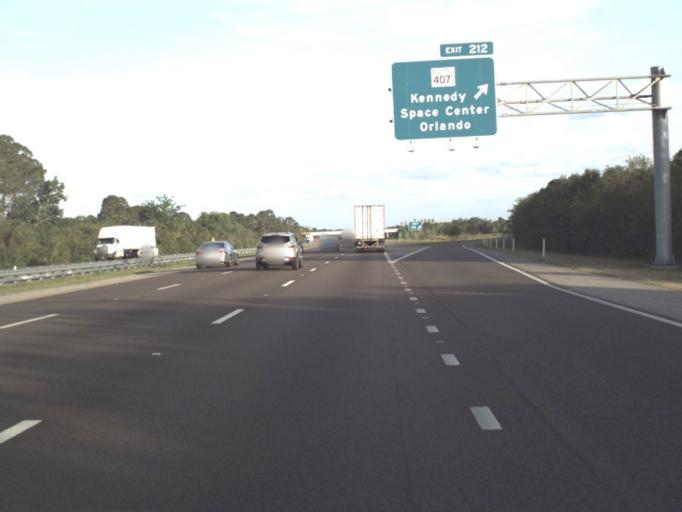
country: US
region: Florida
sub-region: Brevard County
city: Port Saint John
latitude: 28.5074
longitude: -80.8436
